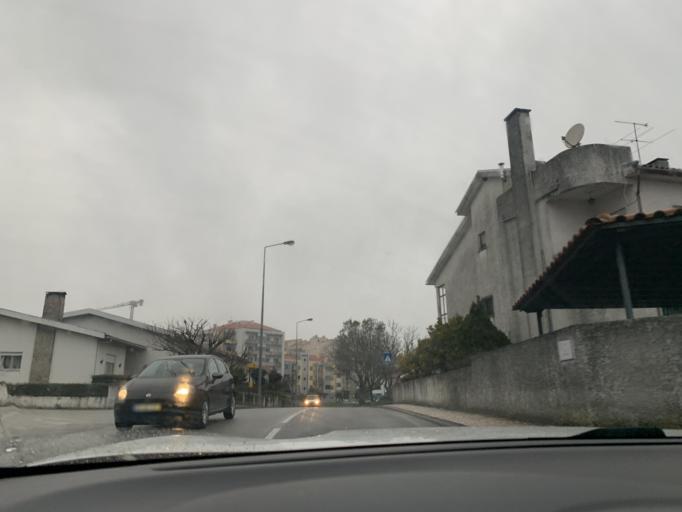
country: PT
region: Viseu
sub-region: Viseu
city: Viseu
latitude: 40.6463
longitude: -7.9065
